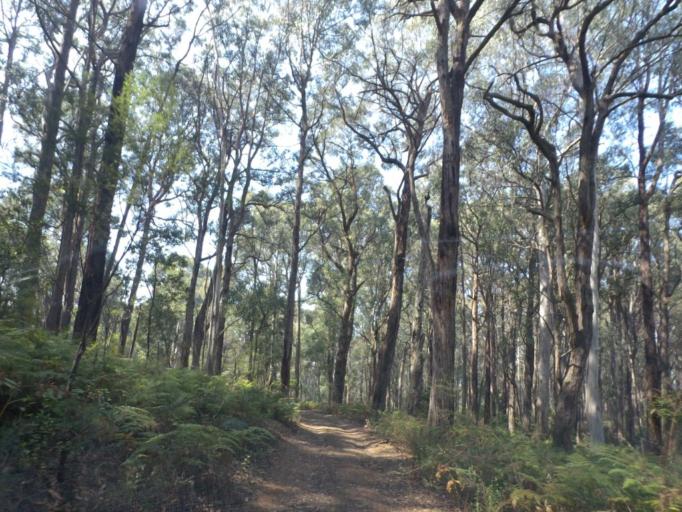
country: AU
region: Victoria
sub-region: Yarra Ranges
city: Healesville
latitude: -37.5600
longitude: 145.6318
